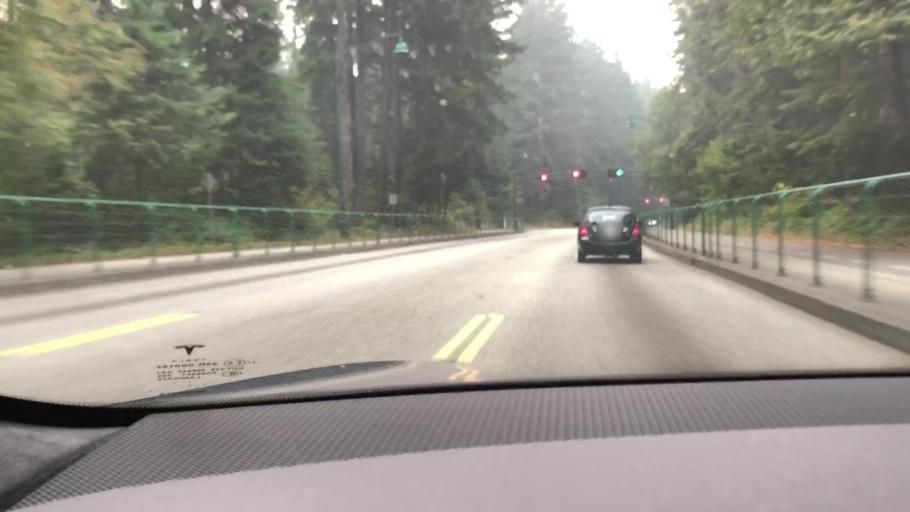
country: CA
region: British Columbia
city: West End
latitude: 49.3011
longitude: -123.1434
